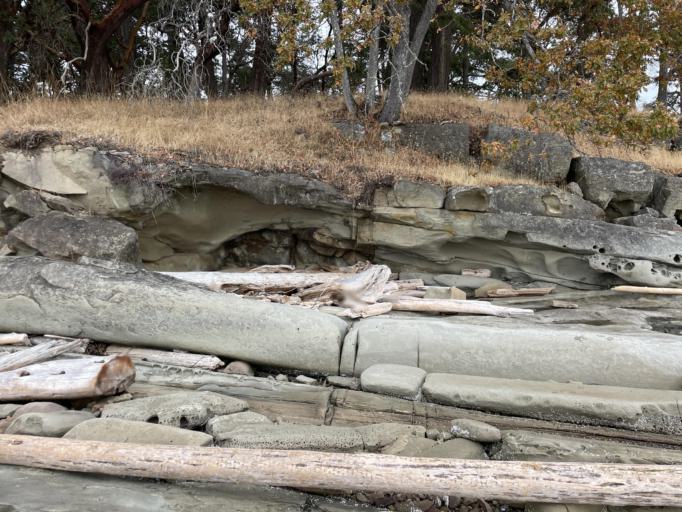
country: CA
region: British Columbia
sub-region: Cowichan Valley Regional District
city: Ladysmith
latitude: 49.0923
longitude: -123.7205
